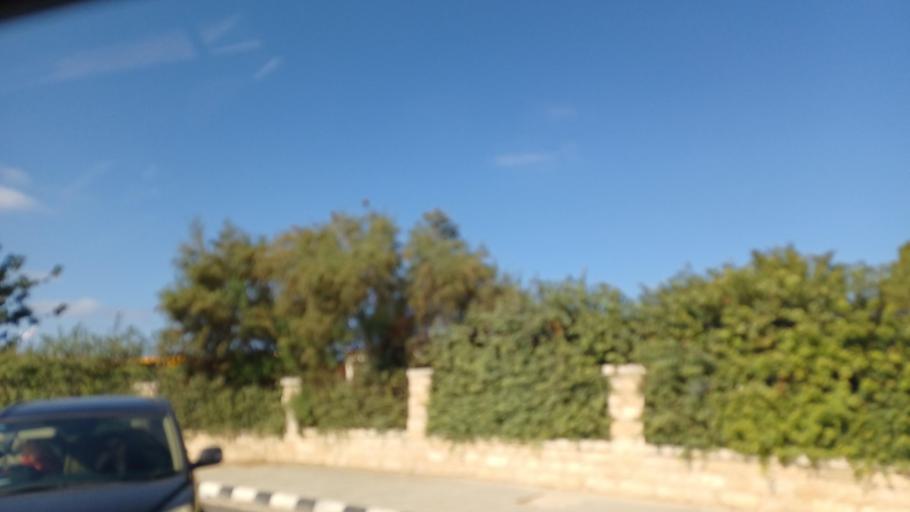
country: CY
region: Pafos
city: Polis
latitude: 35.0386
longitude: 32.4346
